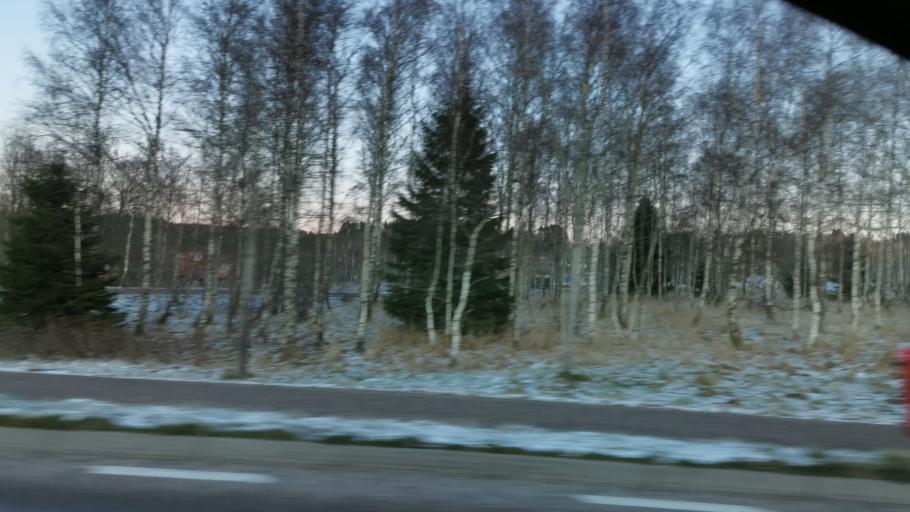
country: SE
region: Vaestra Goetaland
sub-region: Munkedals Kommun
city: Munkedal
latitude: 58.3985
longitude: 11.7504
